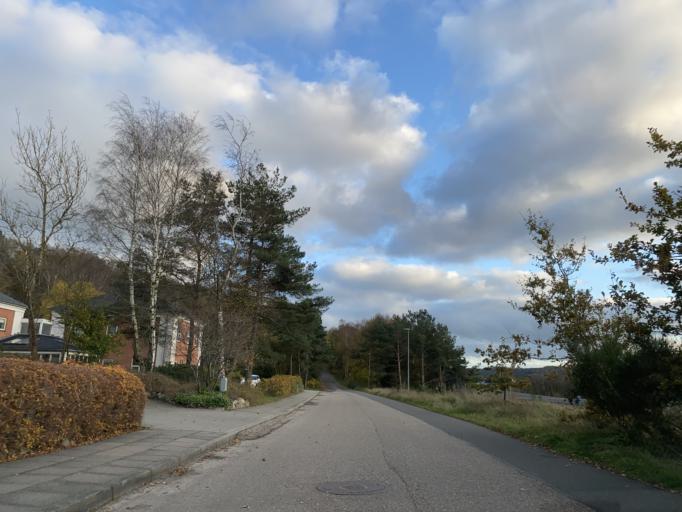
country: DK
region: Central Jutland
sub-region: Silkeborg Kommune
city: Silkeborg
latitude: 56.1789
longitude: 9.5932
